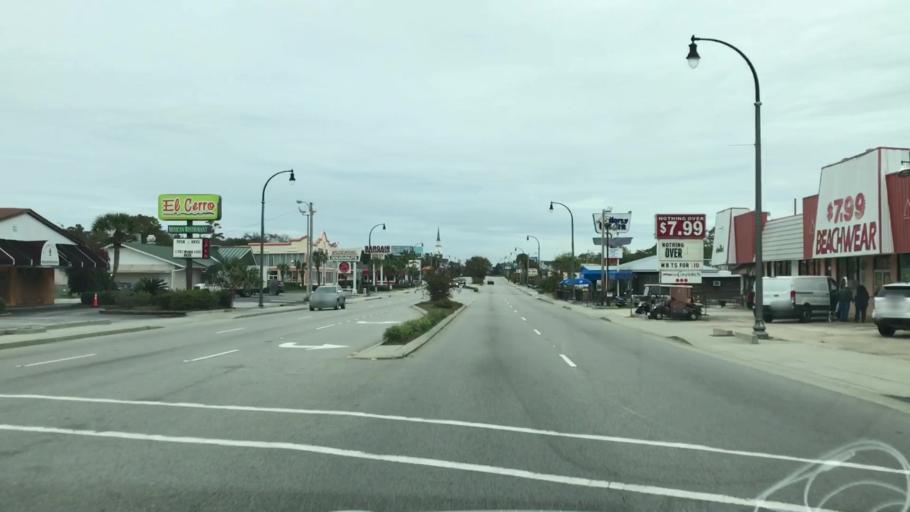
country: US
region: South Carolina
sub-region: Horry County
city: Myrtle Beach
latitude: 33.6853
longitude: -78.8910
